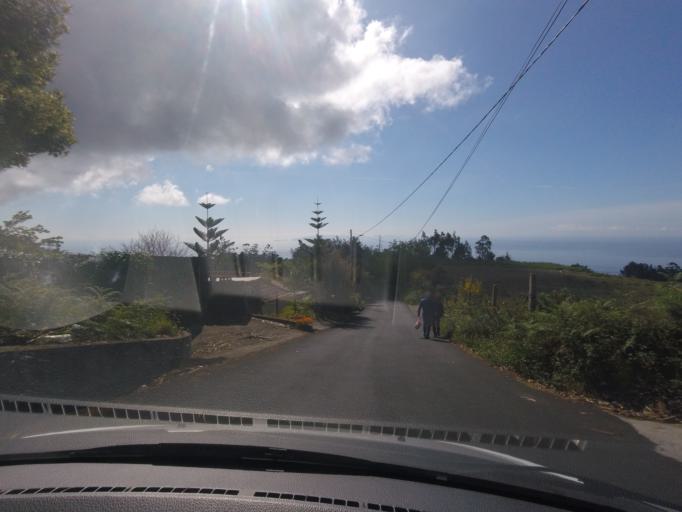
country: PT
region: Madeira
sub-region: Santa Cruz
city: Camacha
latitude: 32.6714
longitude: -16.8590
